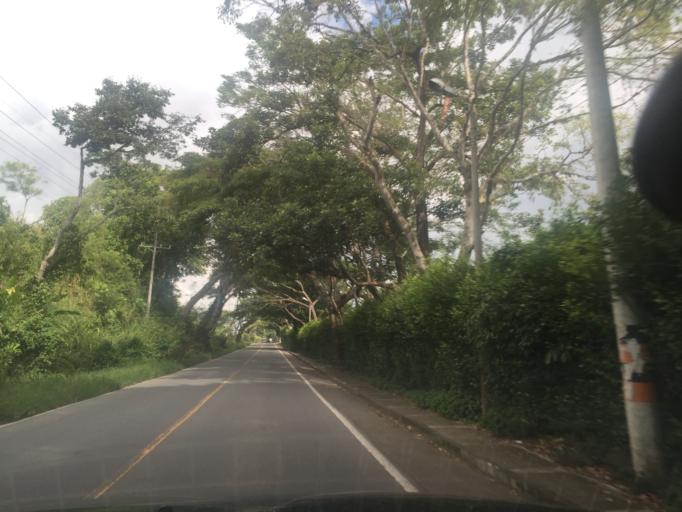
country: CO
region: Valle del Cauca
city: Caicedonia
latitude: 4.3415
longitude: -75.8386
